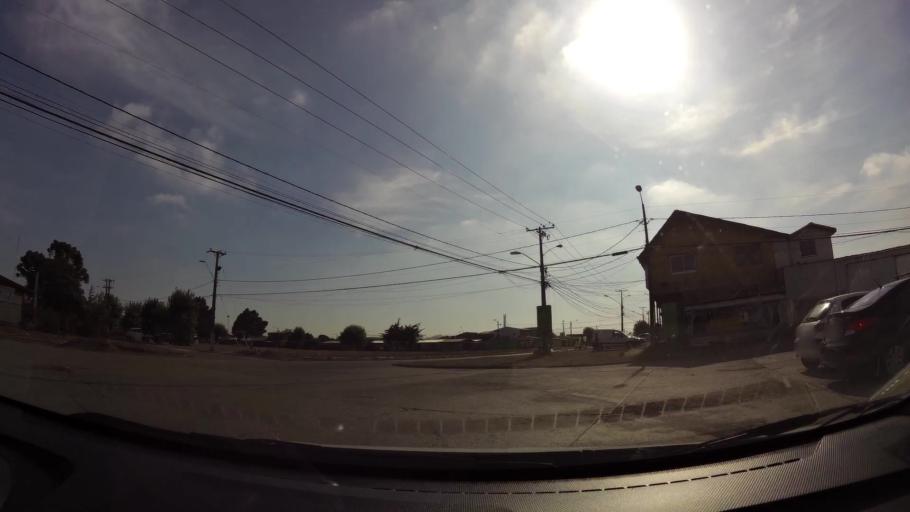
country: CL
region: Biobio
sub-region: Provincia de Concepcion
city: Talcahuano
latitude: -36.7863
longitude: -73.1157
